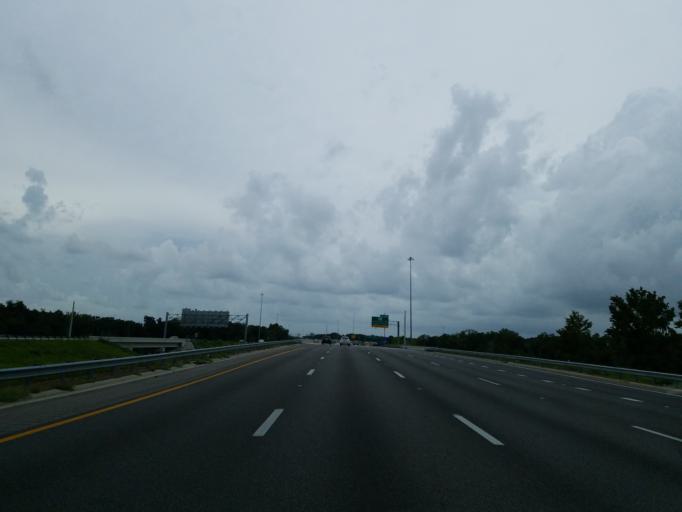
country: US
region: Florida
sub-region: Hillsborough County
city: Temple Terrace
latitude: 28.0628
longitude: -82.3540
